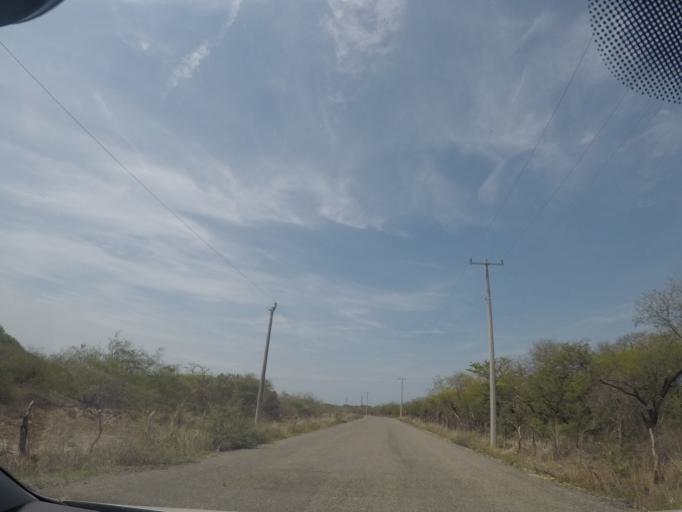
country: MX
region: Oaxaca
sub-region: Salina Cruz
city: Salina Cruz
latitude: 16.2059
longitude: -95.1216
